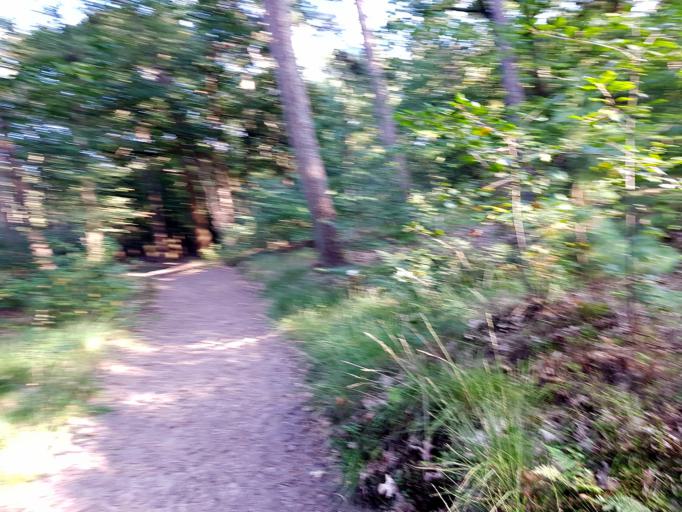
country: NL
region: Utrecht
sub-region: Gemeente Utrechtse Heuvelrug
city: Maarsbergen
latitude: 52.0456
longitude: 5.4328
